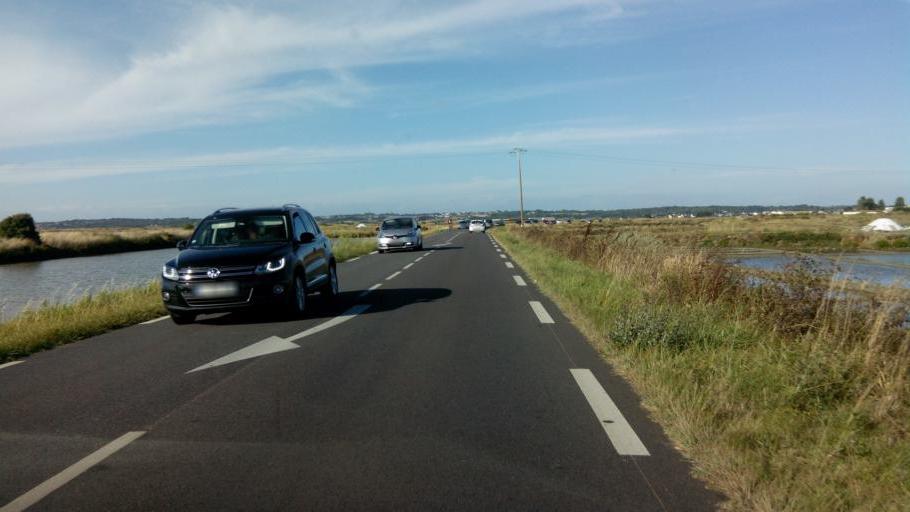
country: FR
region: Pays de la Loire
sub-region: Departement de la Loire-Atlantique
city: Le Pouliguen
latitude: 47.2830
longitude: -2.4523
